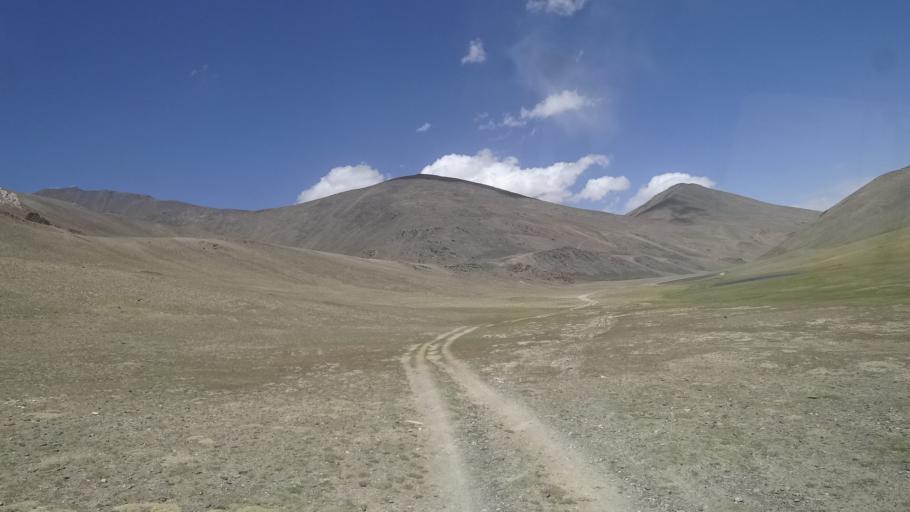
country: TJ
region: Gorno-Badakhshan
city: Murghob
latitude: 37.5163
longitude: 74.0572
